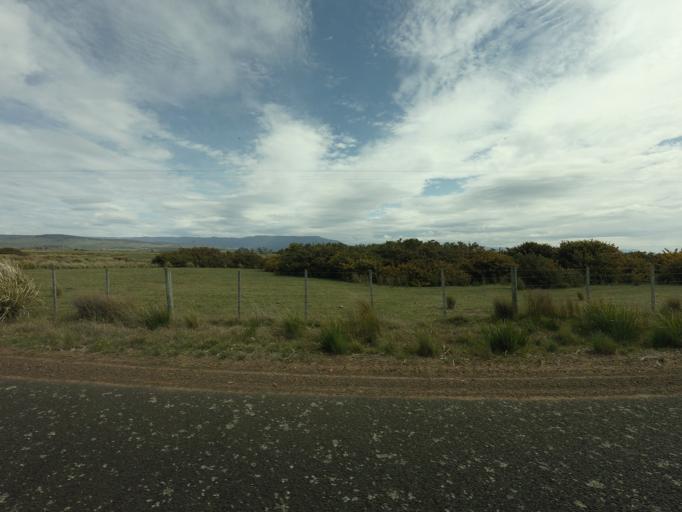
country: AU
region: Tasmania
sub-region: Northern Midlands
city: Evandale
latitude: -41.8361
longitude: 147.3303
